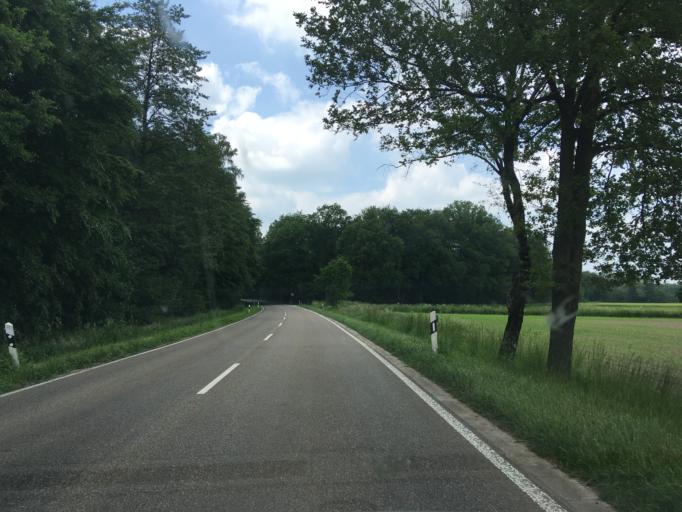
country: DE
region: North Rhine-Westphalia
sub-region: Regierungsbezirk Munster
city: Raesfeld
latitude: 51.7752
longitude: 6.8040
